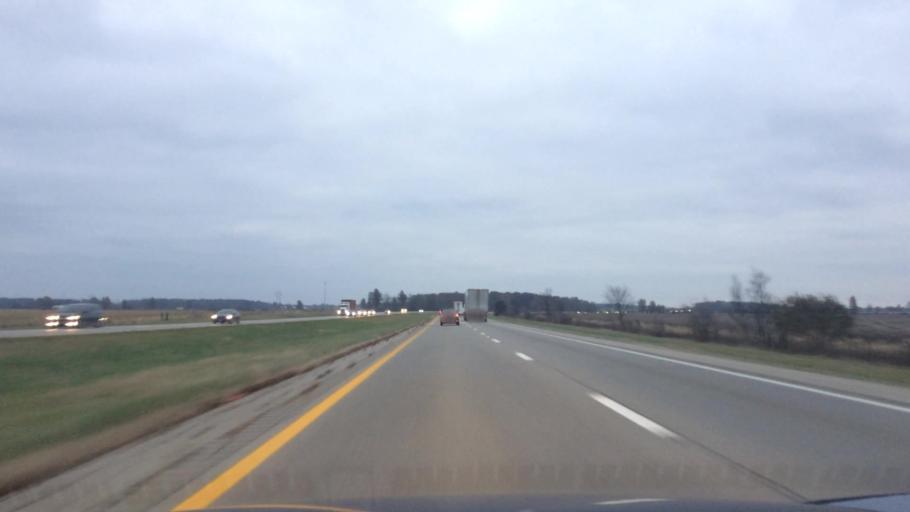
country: US
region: Ohio
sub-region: Union County
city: New California
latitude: 40.1860
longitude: -83.2573
